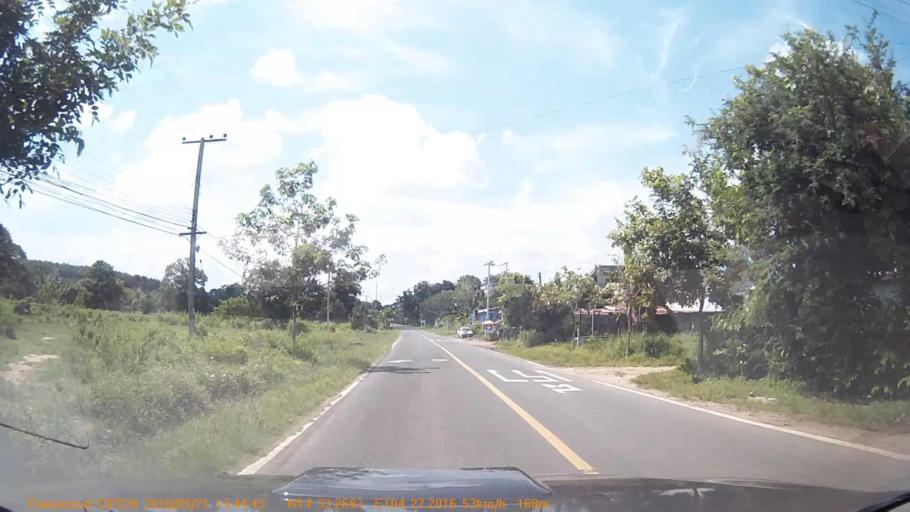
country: TH
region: Sisaket
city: Khun Han
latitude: 14.5548
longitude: 104.4530
